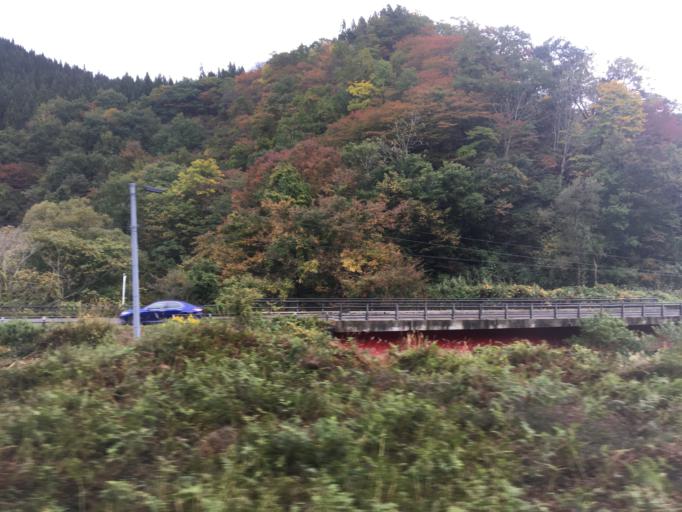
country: JP
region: Yamagata
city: Nagai
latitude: 38.0170
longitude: 139.8936
